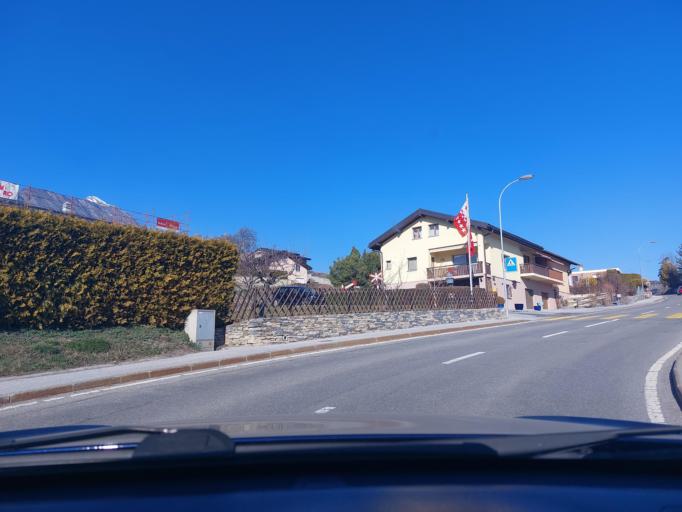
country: CH
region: Valais
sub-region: Sion District
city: Saviese
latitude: 46.2395
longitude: 7.3377
